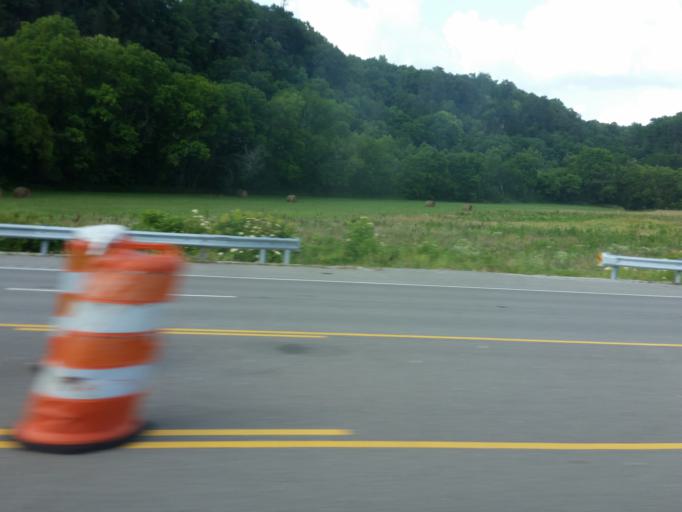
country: US
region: Tennessee
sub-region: Lewis County
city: Hohenwald
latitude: 35.5623
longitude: -87.3963
